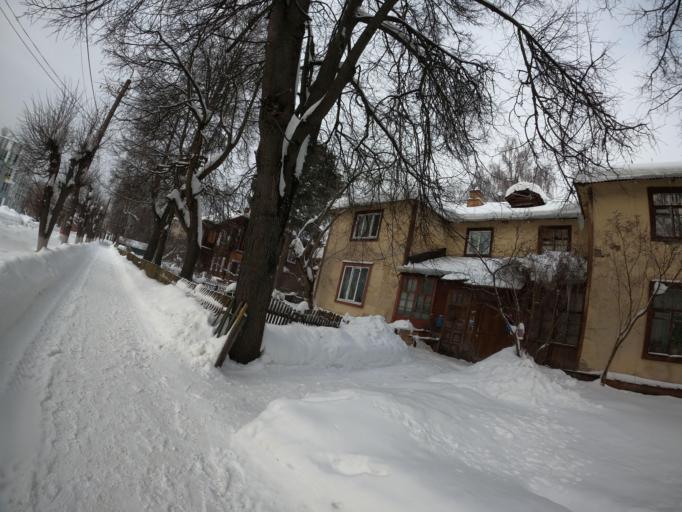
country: RU
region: Moskovskaya
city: Elektrogorsk
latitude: 55.8896
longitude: 38.7756
